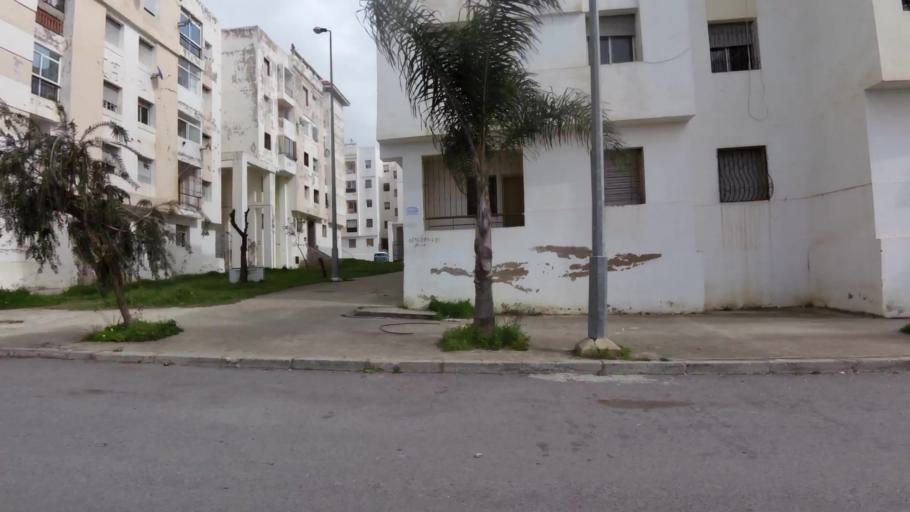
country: MA
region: Tanger-Tetouan
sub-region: Tanger-Assilah
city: Boukhalef
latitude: 35.7419
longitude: -5.8877
